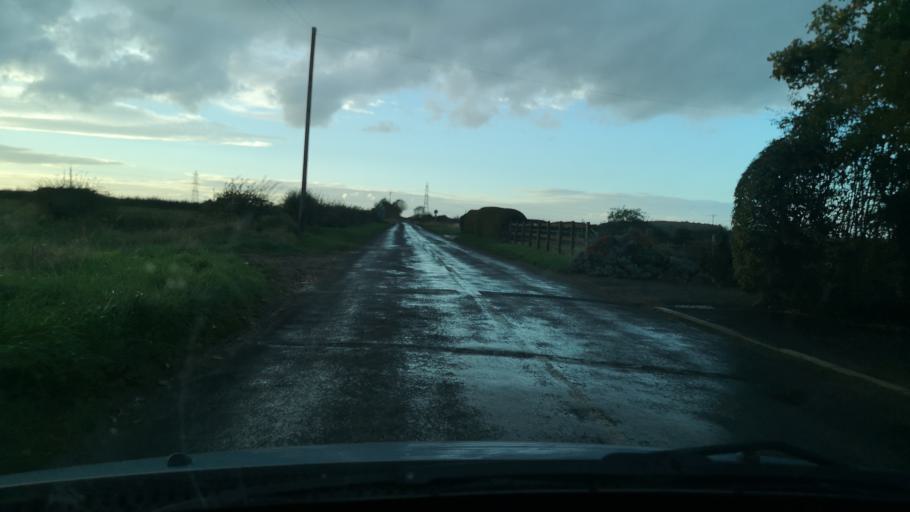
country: GB
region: England
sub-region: Doncaster
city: Norton
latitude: 53.6436
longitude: -1.2228
